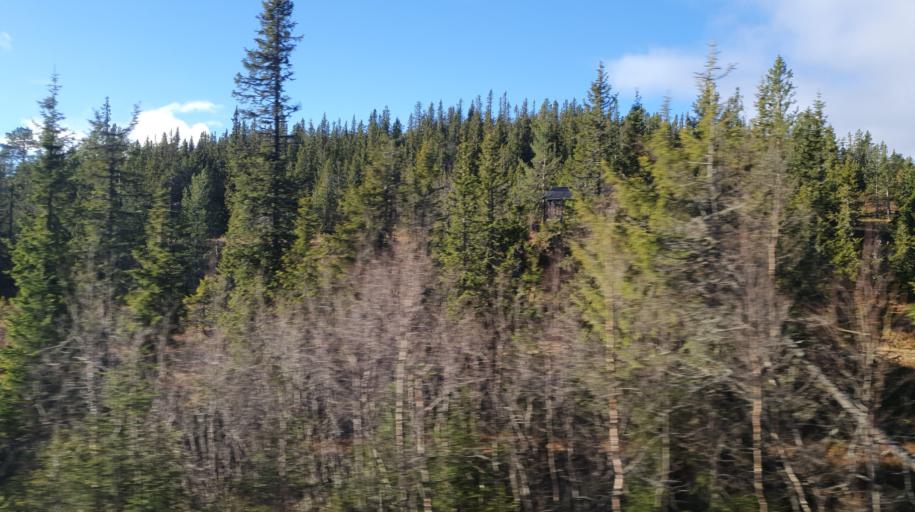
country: NO
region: Buskerud
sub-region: Krodsherad
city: Noresund
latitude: 60.2239
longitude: 9.5293
